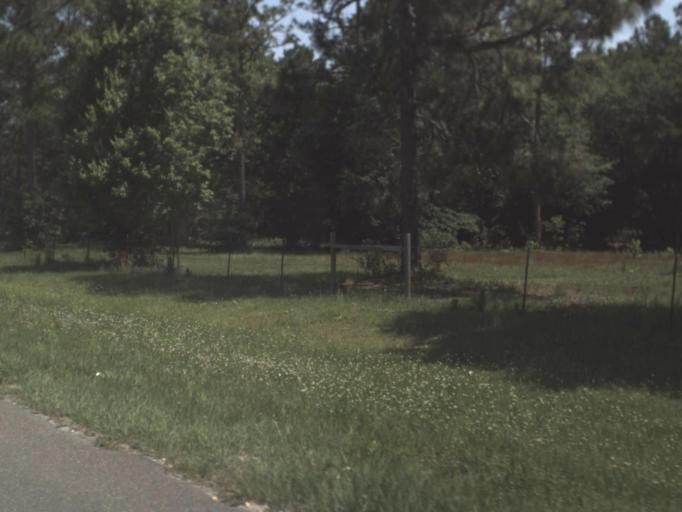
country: US
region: Florida
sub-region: Clay County
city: Keystone Heights
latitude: 29.8522
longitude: -82.0701
